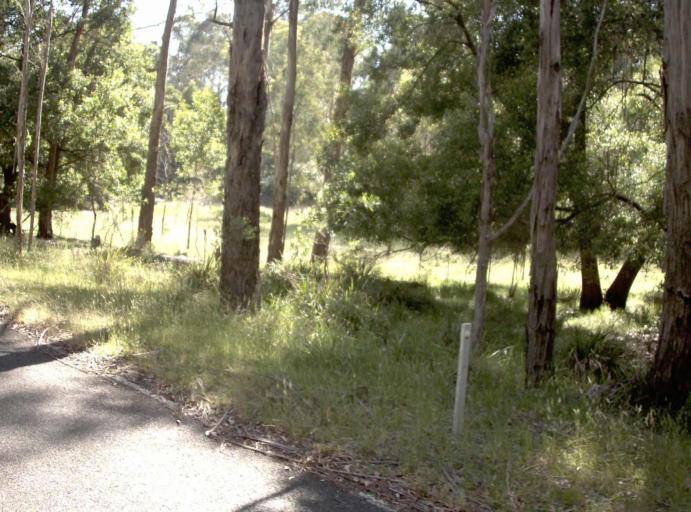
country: AU
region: New South Wales
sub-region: Bombala
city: Bombala
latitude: -37.3690
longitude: 148.6824
